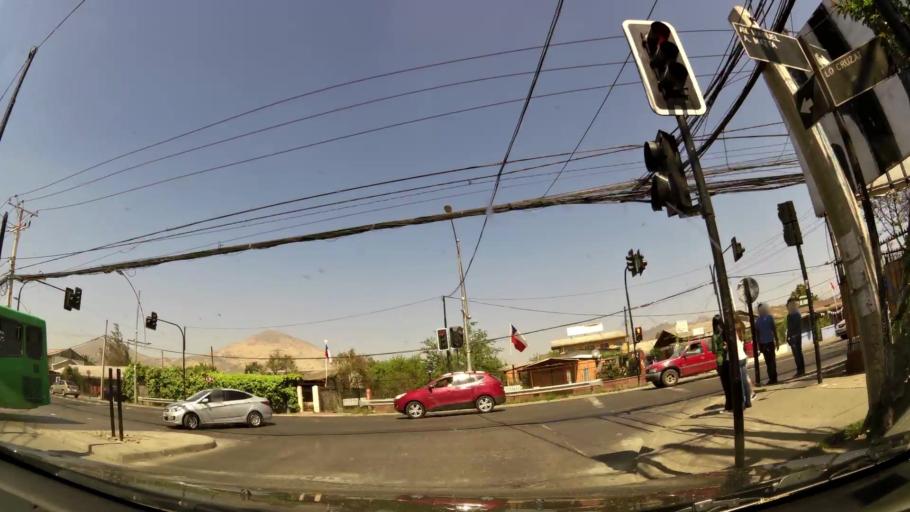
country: CL
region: Santiago Metropolitan
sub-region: Provincia de Santiago
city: Lo Prado
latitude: -33.3664
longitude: -70.7213
